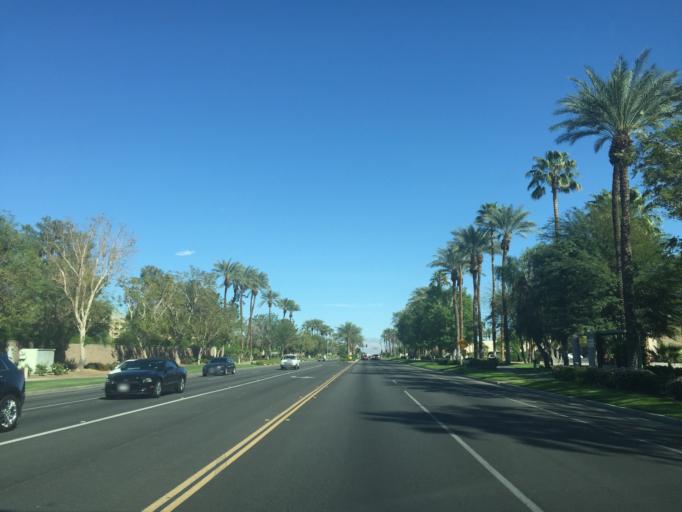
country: US
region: California
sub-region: Riverside County
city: Indian Wells
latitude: 33.7215
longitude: -116.3300
